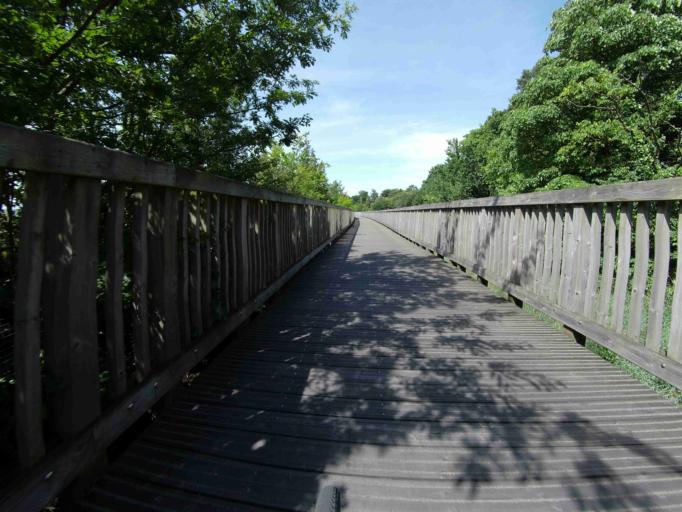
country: GB
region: England
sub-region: Devon
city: Starcross
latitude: 50.6541
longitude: -3.4351
